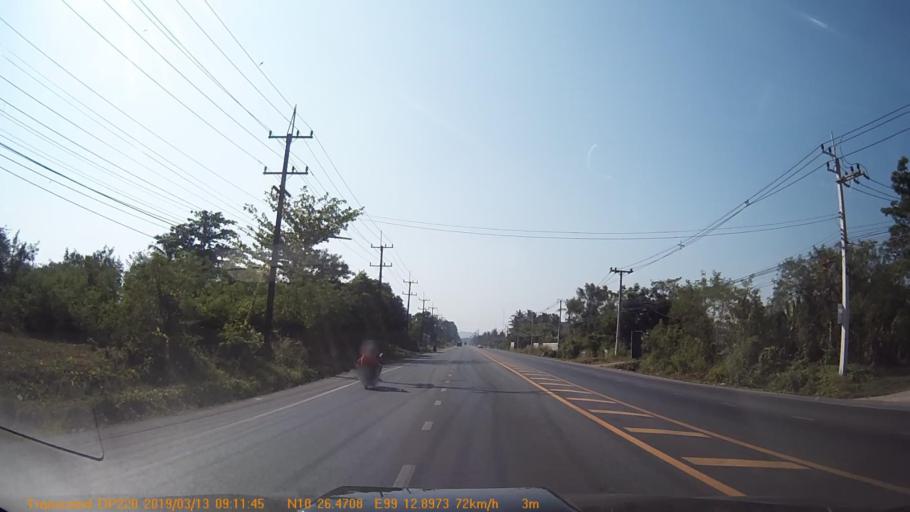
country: TH
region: Chumphon
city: Chumphon
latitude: 10.4409
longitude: 99.2151
